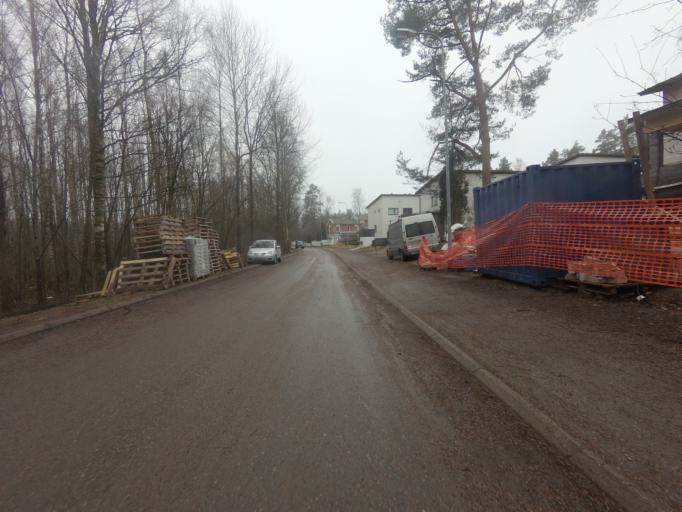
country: FI
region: Uusimaa
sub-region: Helsinki
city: Espoo
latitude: 60.1539
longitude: 24.6936
